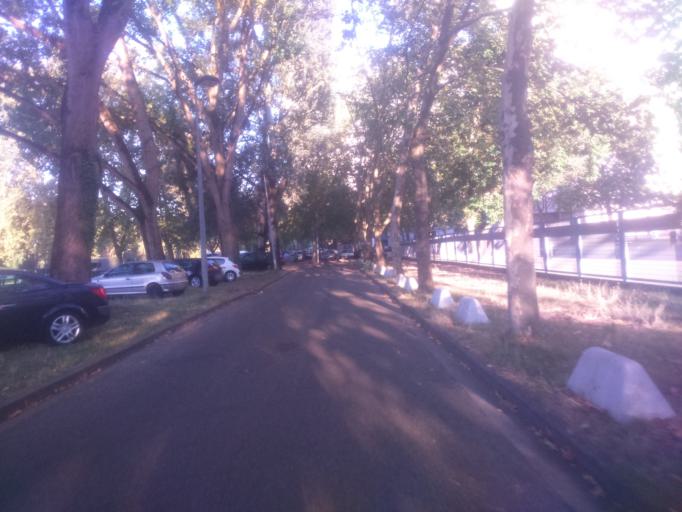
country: FR
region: Aquitaine
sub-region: Departement de la Gironde
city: Le Bouscat
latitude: 44.8724
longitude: -0.5698
